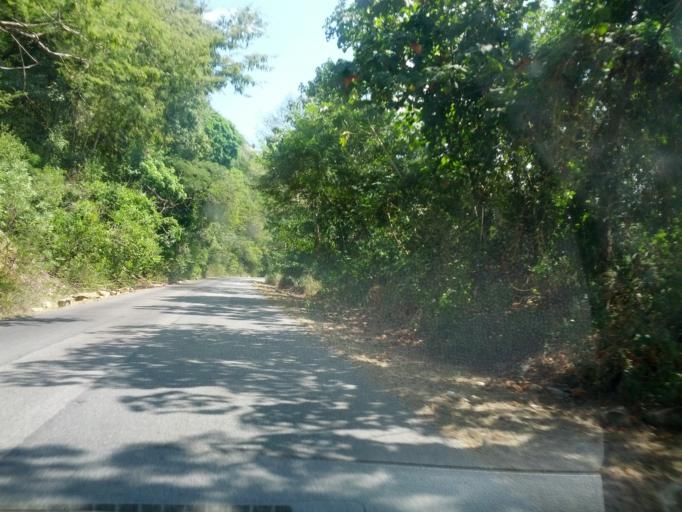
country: CR
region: Puntarenas
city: Ciudad Cortes
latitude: 8.9635
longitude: -83.3164
